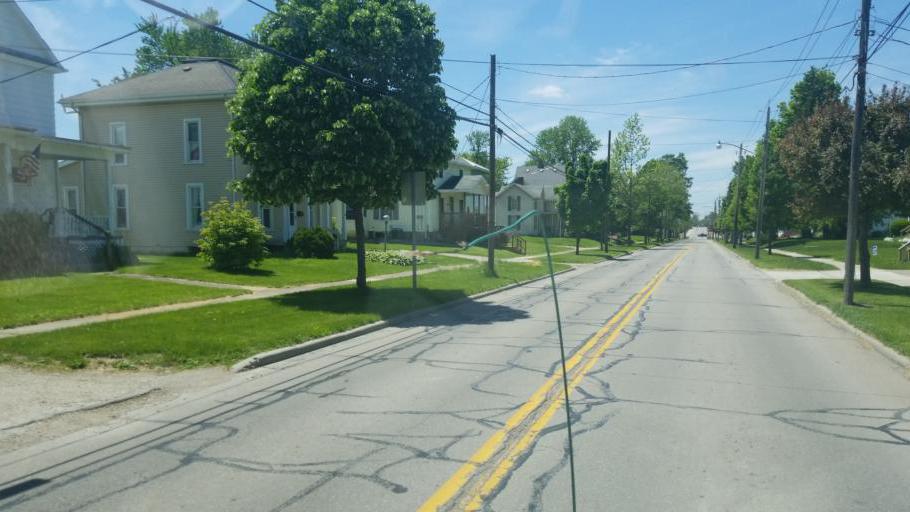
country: US
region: Ohio
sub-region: Huron County
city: Greenwich
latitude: 41.0298
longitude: -82.5110
